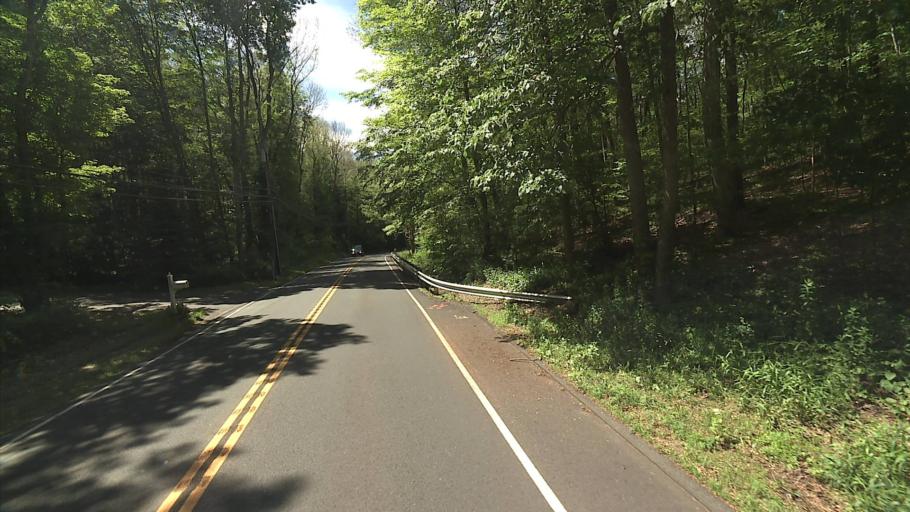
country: US
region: Connecticut
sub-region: Middlesex County
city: Durham
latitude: 41.4063
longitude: -72.6962
